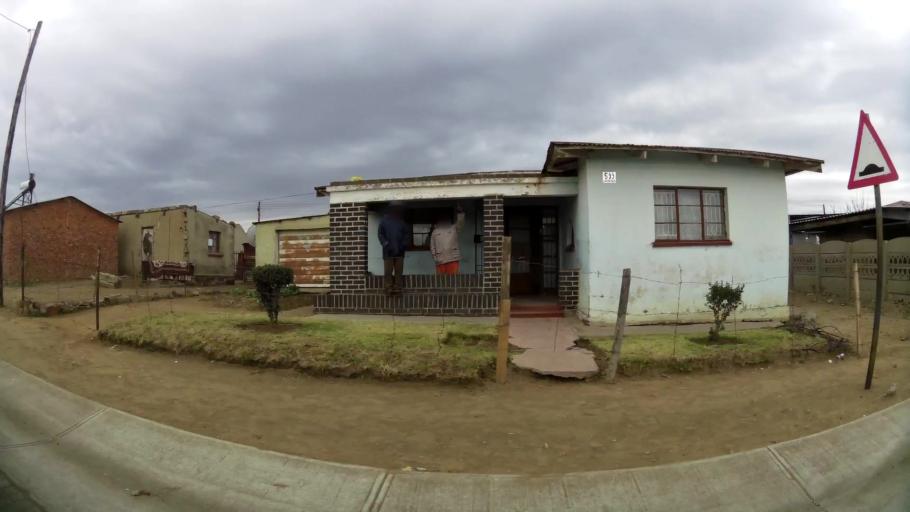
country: ZA
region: Orange Free State
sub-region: Fezile Dabi District Municipality
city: Kroonstad
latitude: -27.6500
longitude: 27.2037
